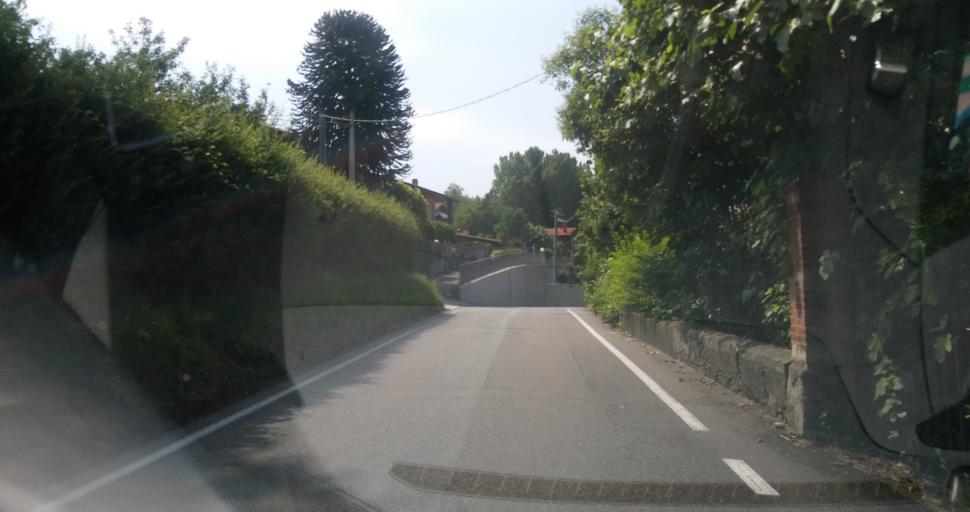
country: IT
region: Lombardy
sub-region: Provincia di Varese
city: Osmate
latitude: 45.7848
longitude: 8.6552
